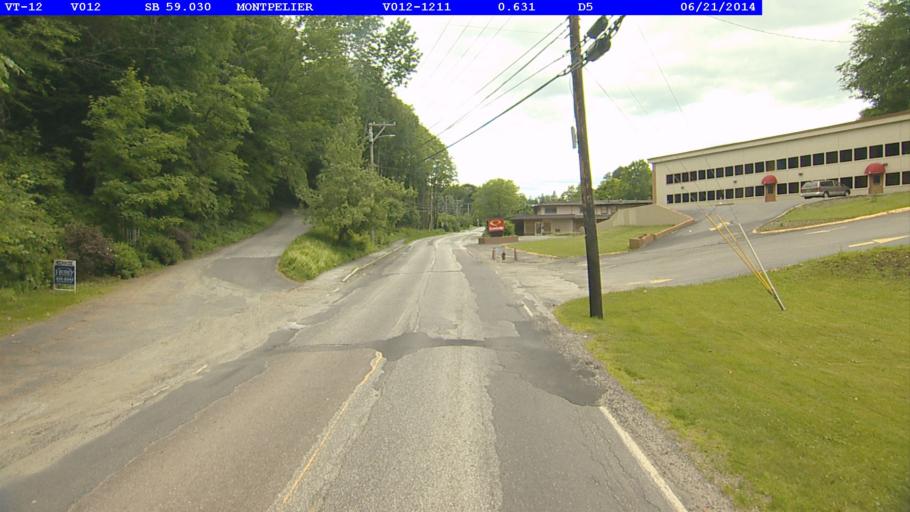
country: US
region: Vermont
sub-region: Washington County
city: Montpelier
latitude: 44.2531
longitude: -72.5807
